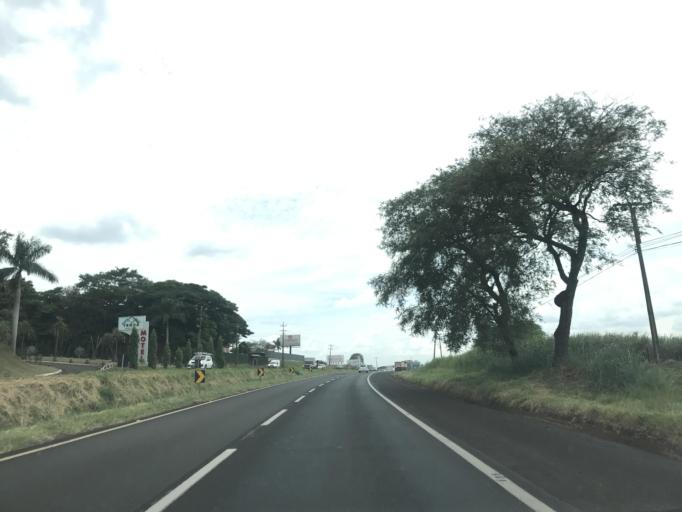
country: BR
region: Parana
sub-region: Paicandu
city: Paicandu
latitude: -23.3906
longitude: -52.0141
